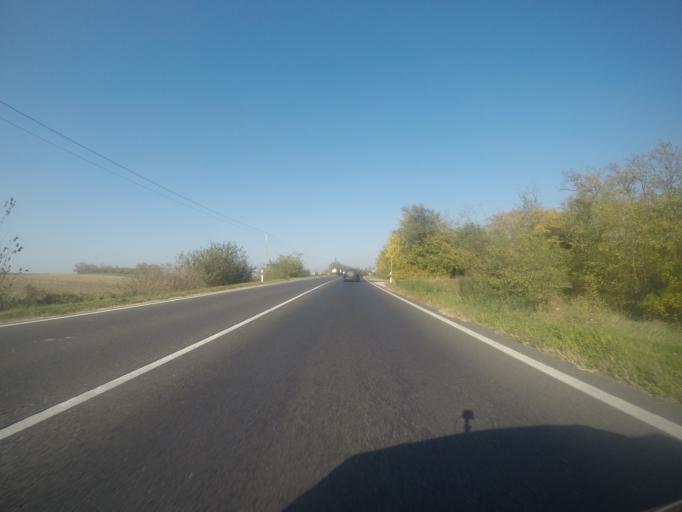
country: HU
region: Fejer
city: Baracs
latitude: 46.8578
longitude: 18.9135
